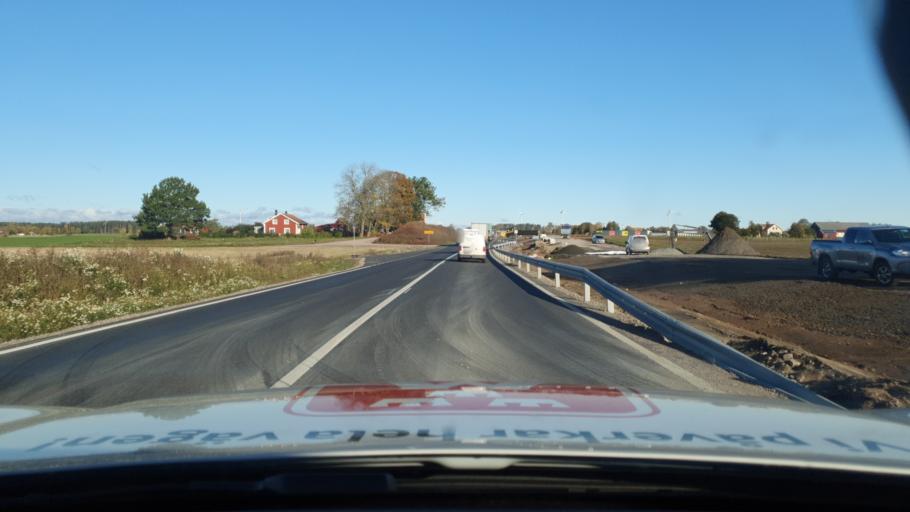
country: SE
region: Vaestra Goetaland
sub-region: Skara Kommun
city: Skara
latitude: 58.4244
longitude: 13.4681
